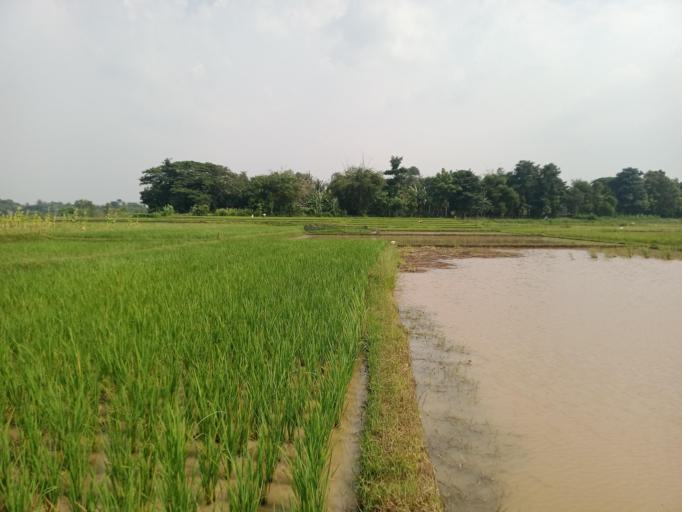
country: ID
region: West Java
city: Kresek
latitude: -6.1367
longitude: 106.4478
